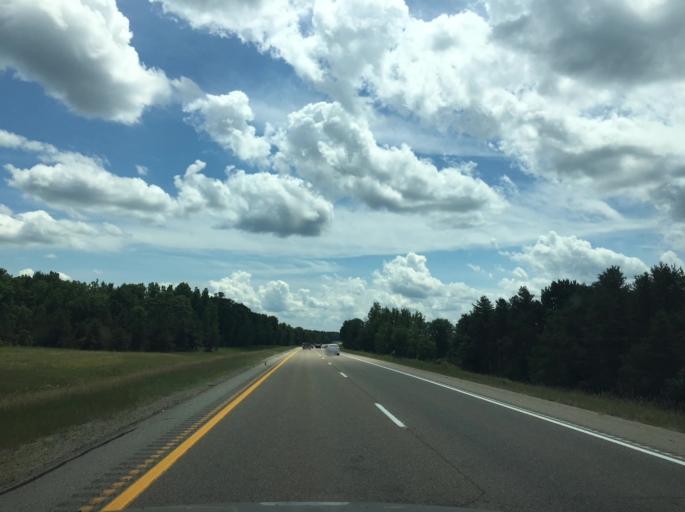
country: US
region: Michigan
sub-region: Crawford County
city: Grayling
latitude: 44.5708
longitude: -84.7092
